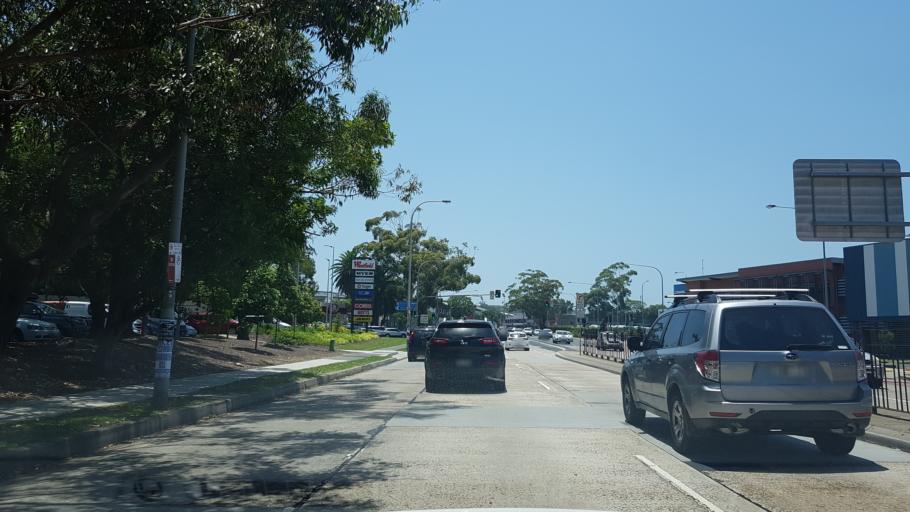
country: AU
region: New South Wales
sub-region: Warringah
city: Brookvale
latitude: -33.7670
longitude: 151.2688
